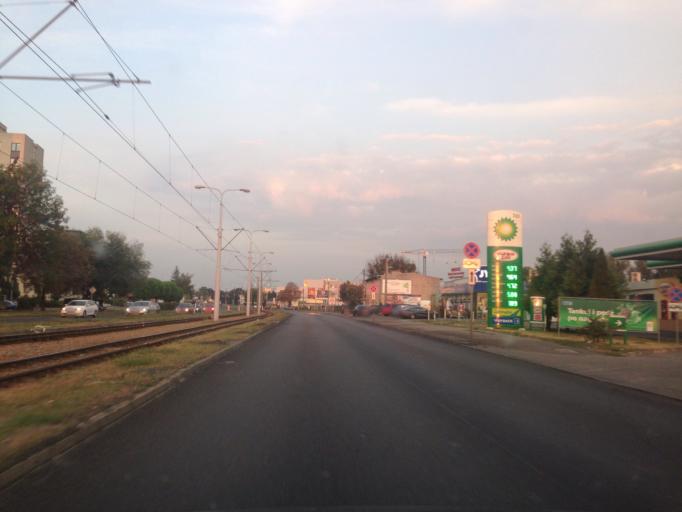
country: PL
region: Kujawsko-Pomorskie
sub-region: Bydgoszcz
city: Bydgoszcz
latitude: 53.1205
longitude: 18.0504
